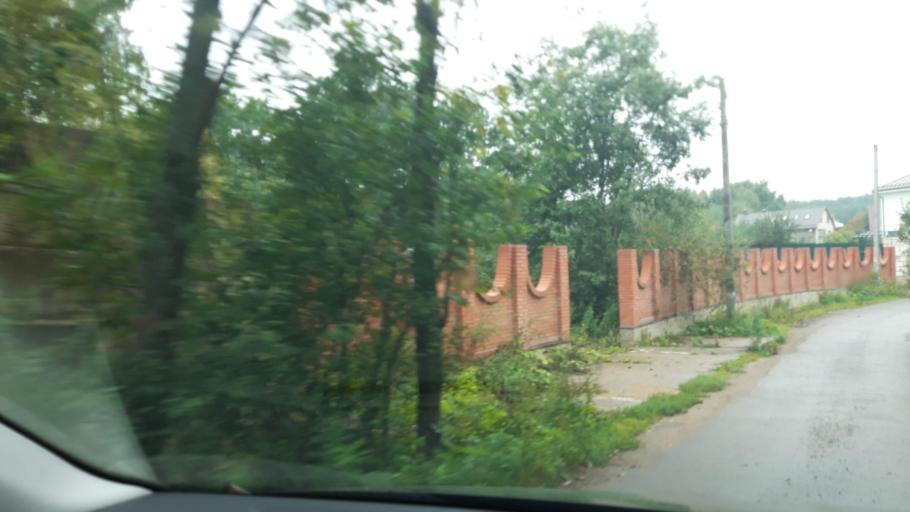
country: RU
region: Moskovskaya
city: Novopodrezkovo
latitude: 55.9238
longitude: 37.3408
